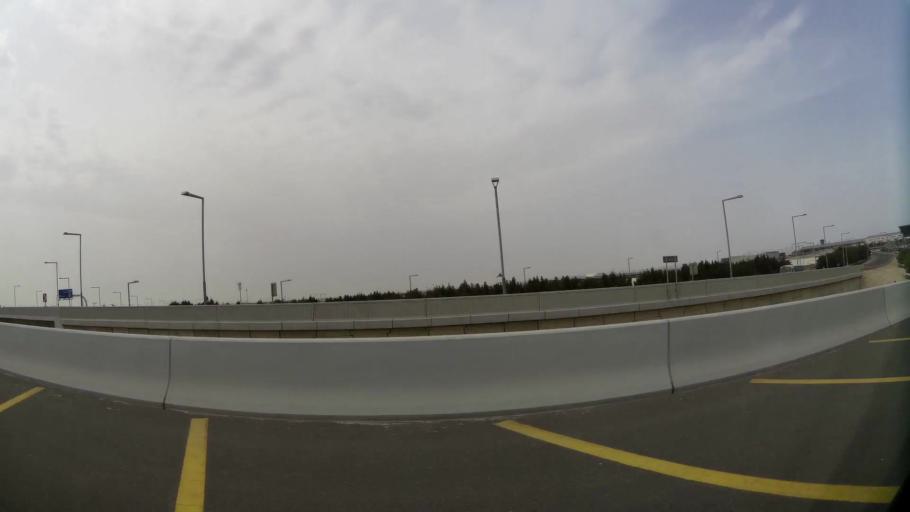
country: QA
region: Al Wakrah
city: Al Wakrah
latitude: 25.2521
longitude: 51.6178
